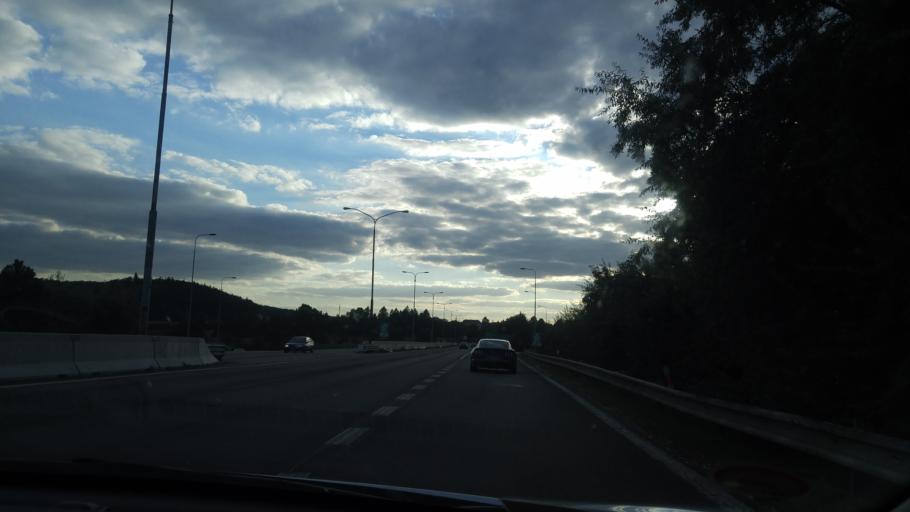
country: CZ
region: South Moravian
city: Ostopovice
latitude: 49.1688
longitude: 16.5490
